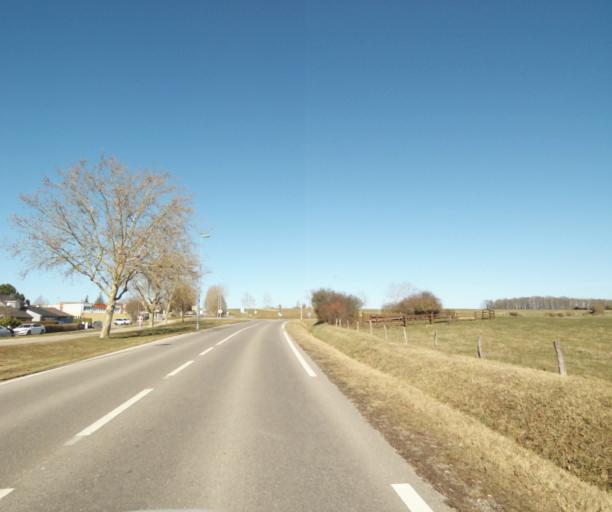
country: FR
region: Lorraine
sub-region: Departement de Meurthe-et-Moselle
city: Heillecourt
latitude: 48.6424
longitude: 6.2109
